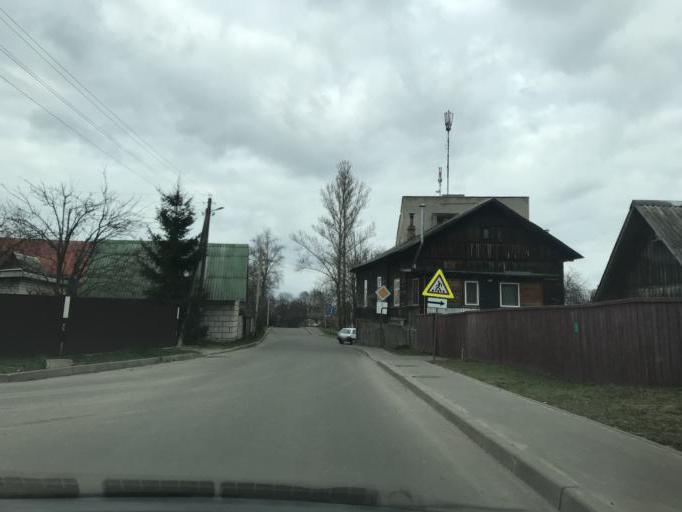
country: BY
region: Mogilev
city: Mahilyow
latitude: 53.8989
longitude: 30.3210
